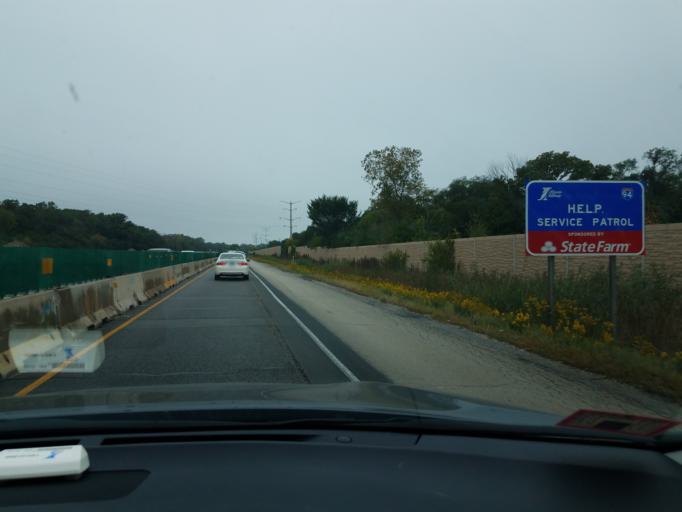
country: US
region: Illinois
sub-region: Cook County
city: Northbrook
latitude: 42.1453
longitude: -87.8182
